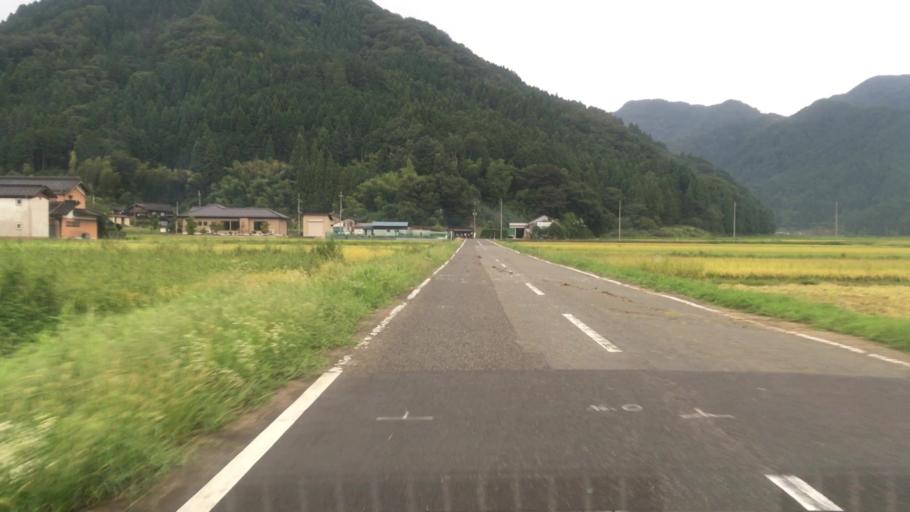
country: JP
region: Hyogo
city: Toyooka
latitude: 35.4542
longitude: 134.7342
